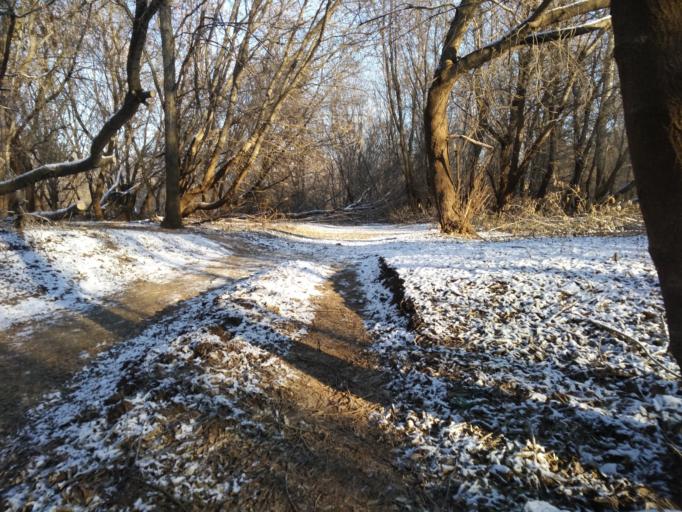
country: RU
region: Kirov
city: Vyatskiye Polyany
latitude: 56.2375
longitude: 51.0796
